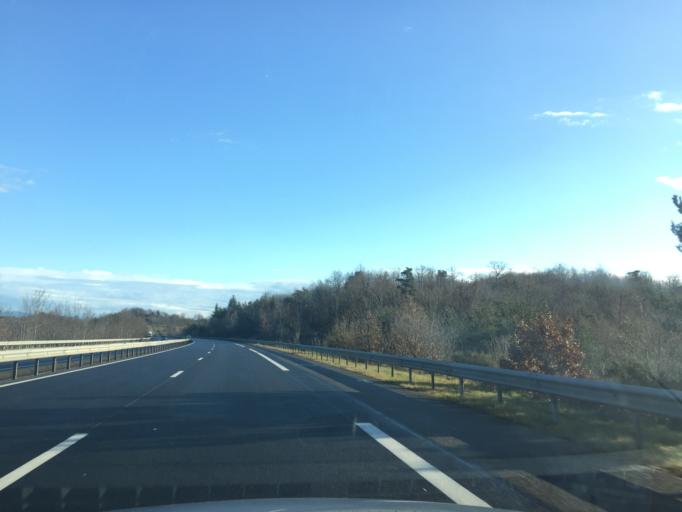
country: FR
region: Rhone-Alpes
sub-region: Departement de la Loire
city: Saint-Germain-Laval
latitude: 45.8602
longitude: 3.9709
